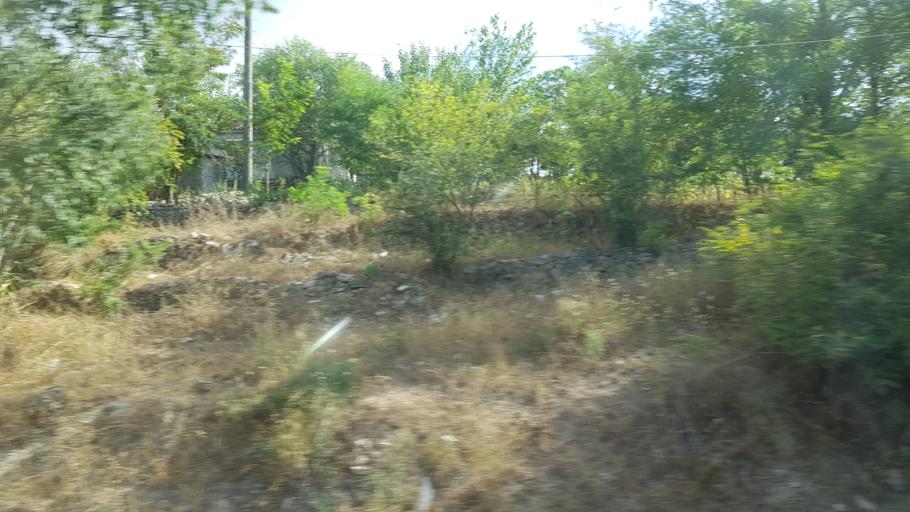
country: AL
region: Vlore
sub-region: Rrethi i Delvines
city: Mesopotam
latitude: 39.9093
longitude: 20.0927
